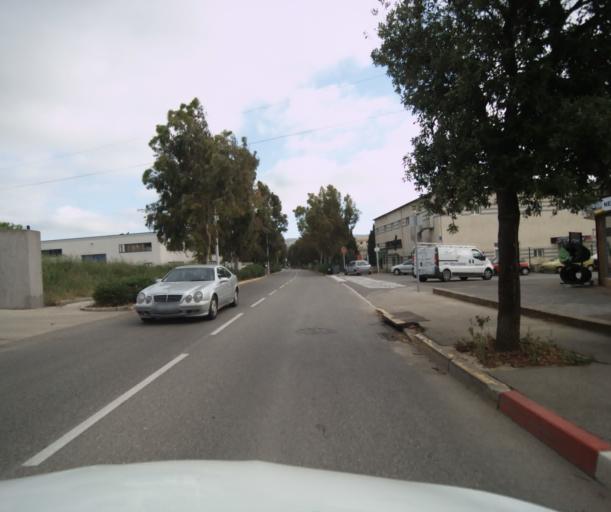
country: FR
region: Provence-Alpes-Cote d'Azur
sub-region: Departement du Var
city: Six-Fours-les-Plages
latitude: 43.1155
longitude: 5.8424
